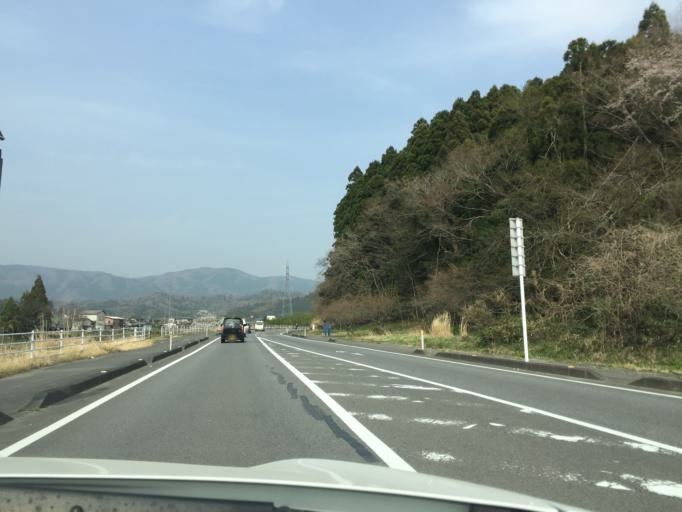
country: JP
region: Fukushima
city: Iwaki
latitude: 37.0026
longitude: 140.7281
